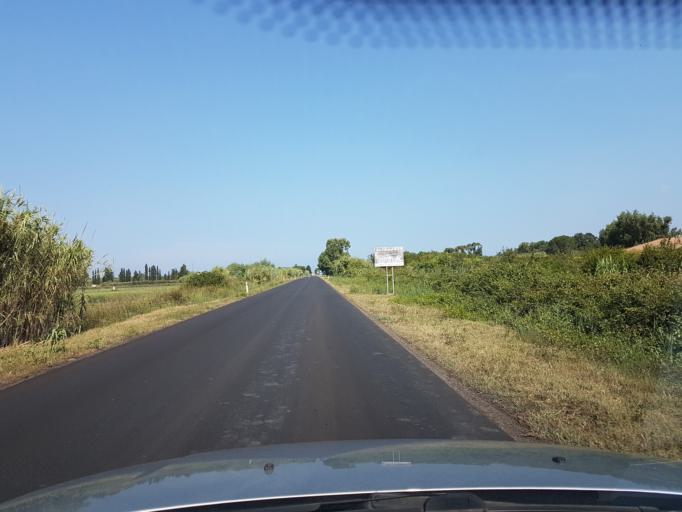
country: IT
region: Sardinia
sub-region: Provincia di Oristano
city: Donigala Fenugheddu
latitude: 39.9483
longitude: 8.5635
